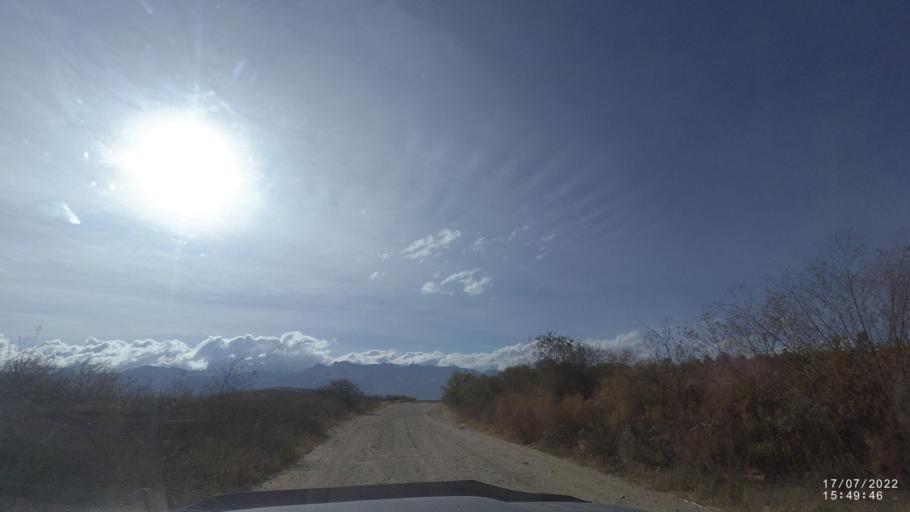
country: BO
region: Cochabamba
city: Sipe Sipe
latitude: -17.4478
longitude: -66.2866
